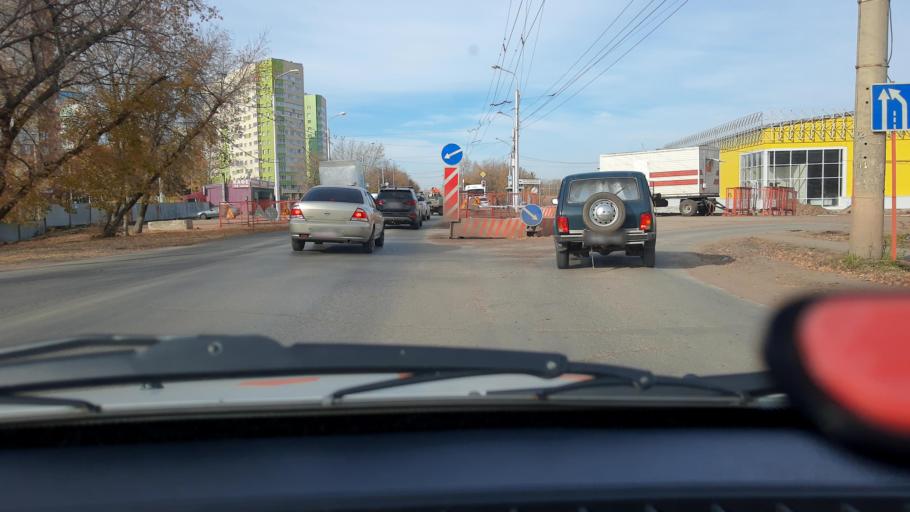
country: RU
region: Bashkortostan
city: Mikhaylovka
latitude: 54.7945
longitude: 55.8731
